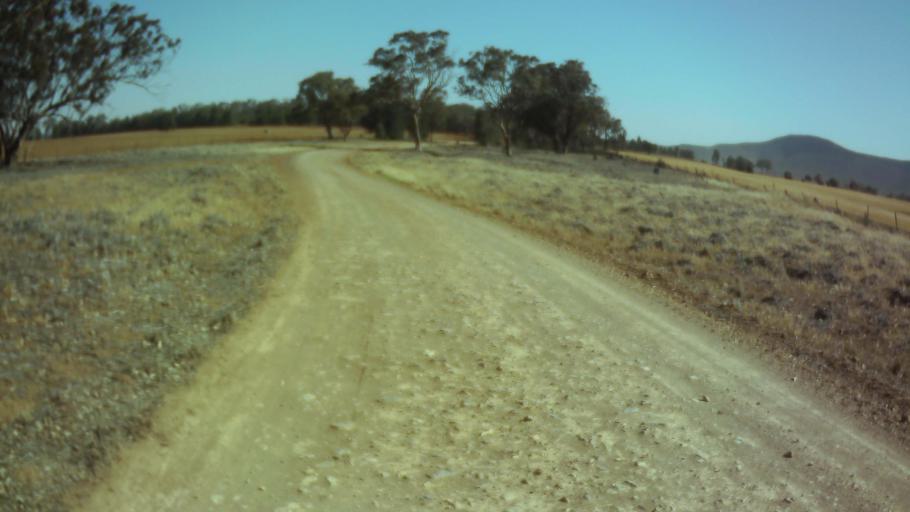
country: AU
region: New South Wales
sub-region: Weddin
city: Grenfell
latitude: -33.8562
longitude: 148.0156
